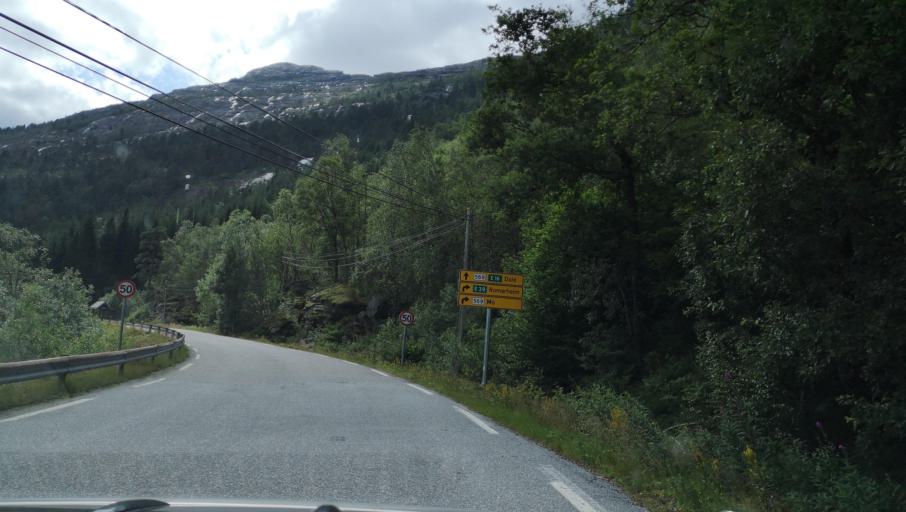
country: NO
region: Hordaland
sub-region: Modalen
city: Mo
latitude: 60.7854
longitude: 5.8402
